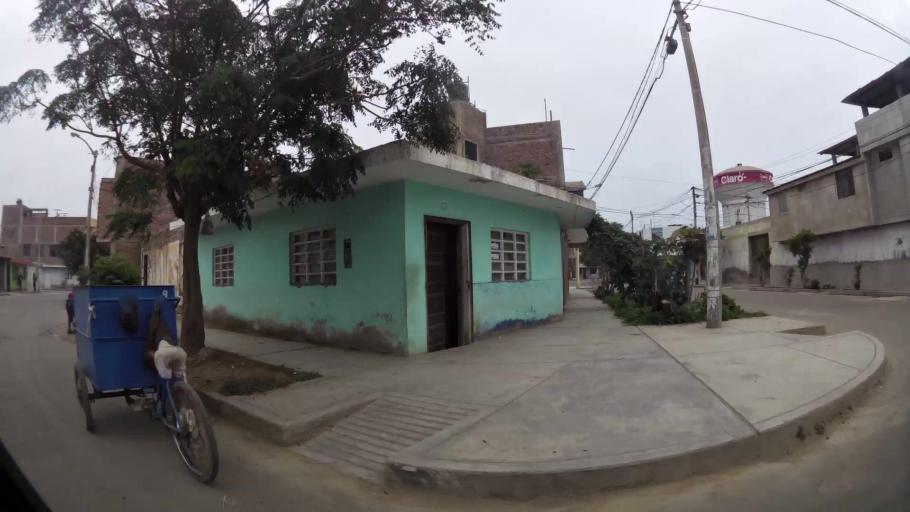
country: PE
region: La Libertad
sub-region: Provincia de Trujillo
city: Buenos Aires
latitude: -8.1412
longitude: -79.0487
